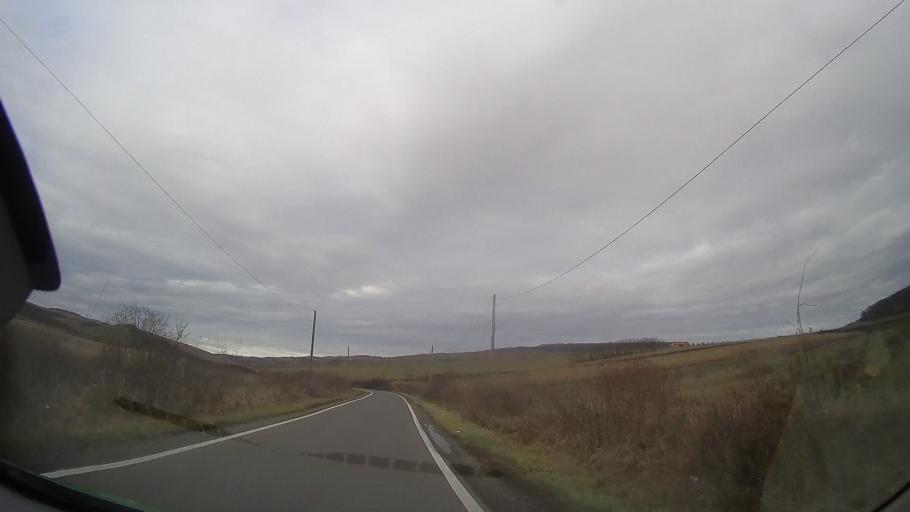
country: RO
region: Mures
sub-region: Comuna Cozma
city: Cozma
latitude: 46.7884
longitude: 24.5466
